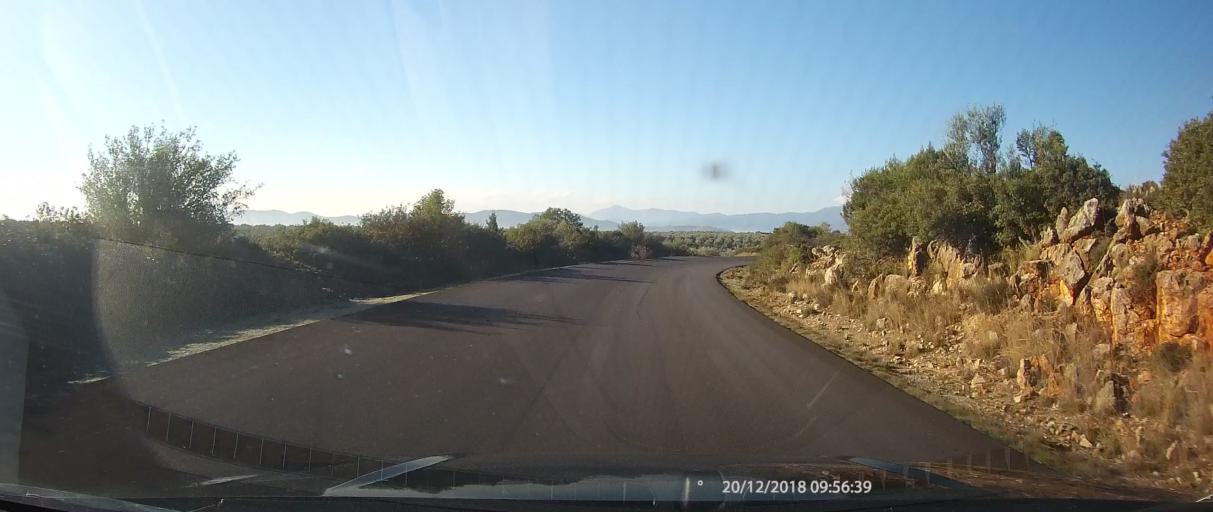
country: GR
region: Peloponnese
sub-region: Nomos Lakonias
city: Yerakion
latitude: 37.0207
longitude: 22.6095
